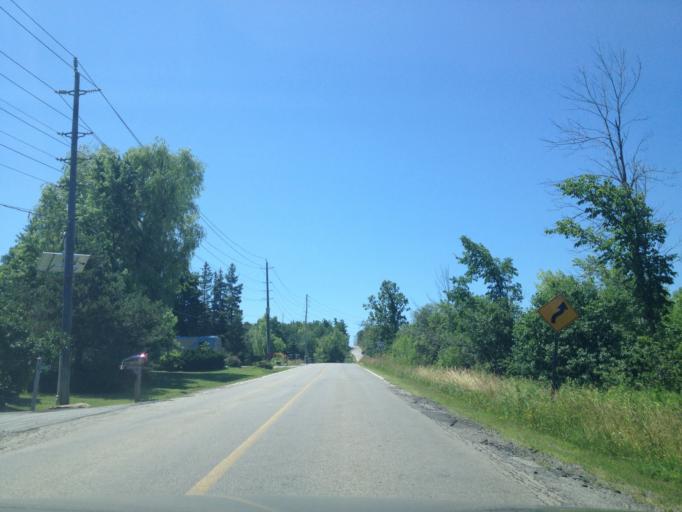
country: CA
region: Ontario
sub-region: Halton
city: Milton
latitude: 43.6625
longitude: -79.9515
